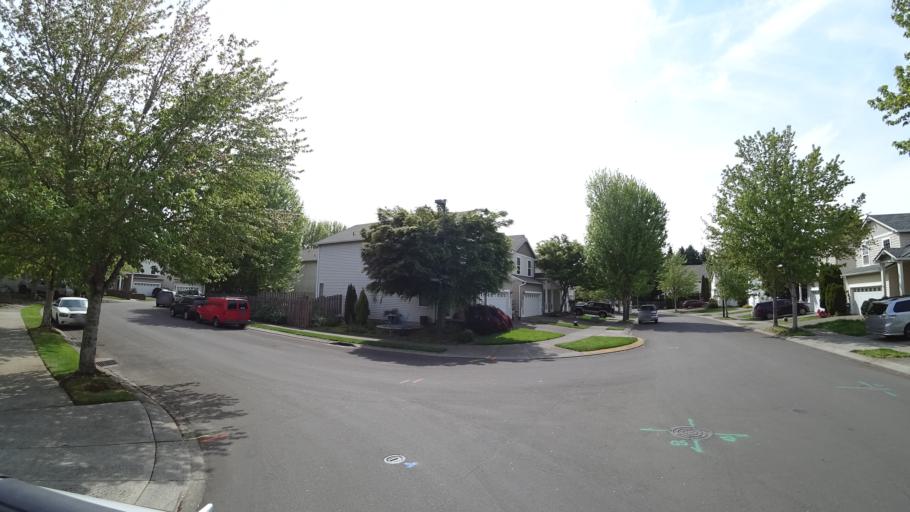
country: US
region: Oregon
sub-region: Washington County
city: Hillsboro
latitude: 45.5216
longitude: -122.9304
